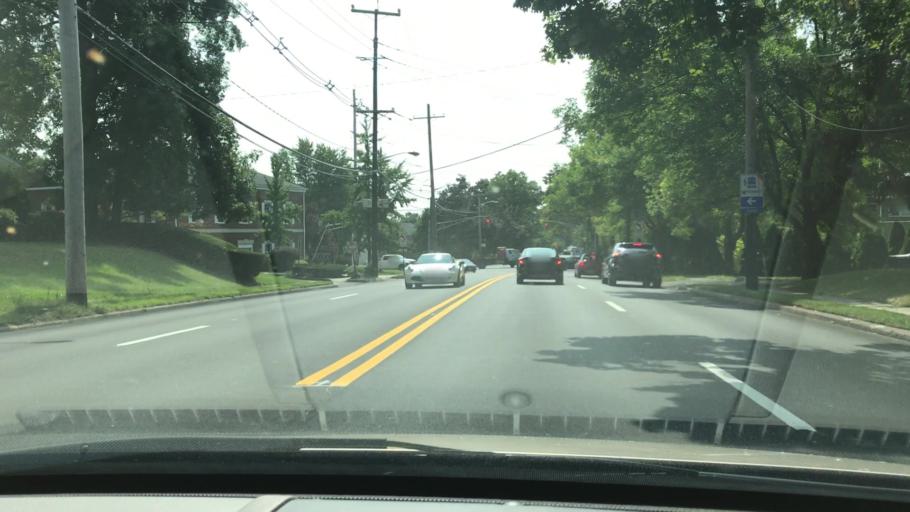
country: US
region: New Jersey
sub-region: Bergen County
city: Oradell
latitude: 40.9559
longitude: -74.0512
